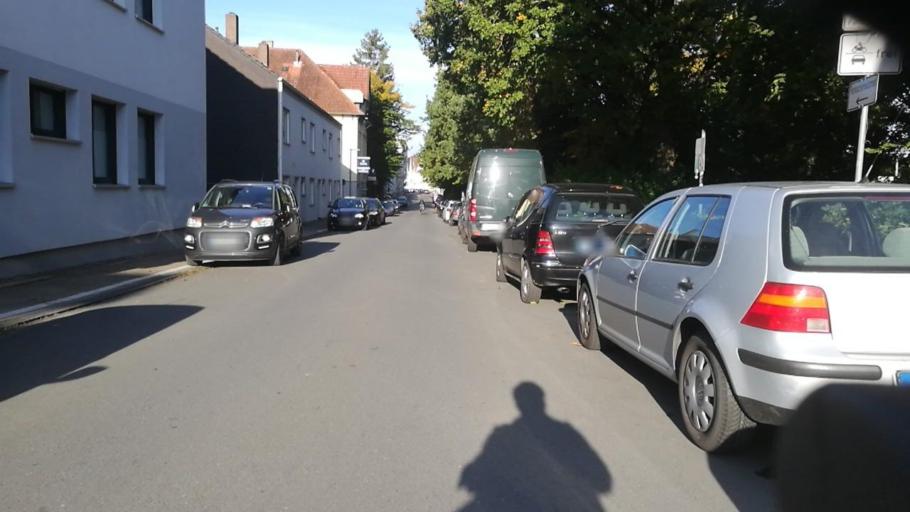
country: DE
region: North Rhine-Westphalia
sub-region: Regierungsbezirk Detmold
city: Bielefeld
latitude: 52.0124
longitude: 8.5446
